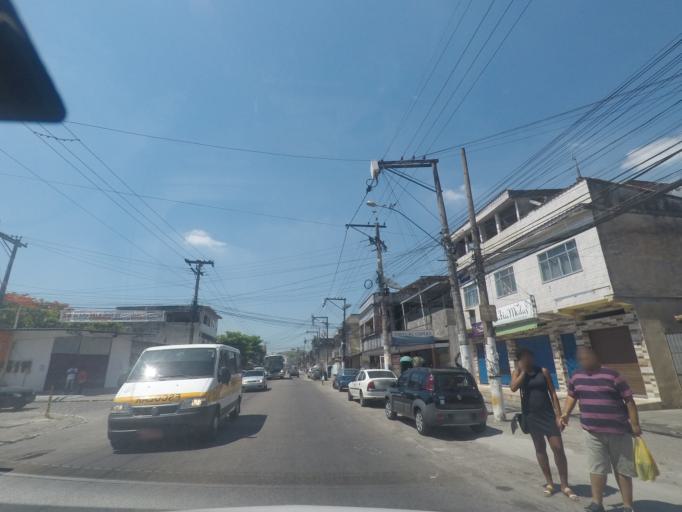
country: BR
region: Rio de Janeiro
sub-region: Petropolis
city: Petropolis
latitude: -22.5909
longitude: -43.1865
